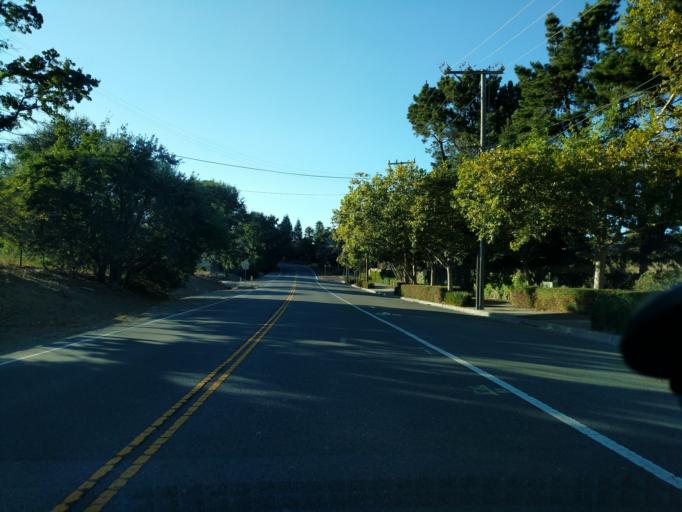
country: US
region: California
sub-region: Alameda County
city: Dublin
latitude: 37.6811
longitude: -121.9237
